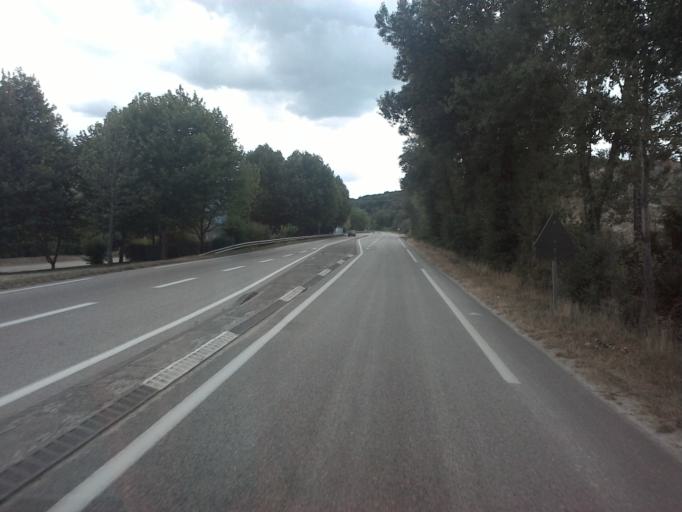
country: FR
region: Rhone-Alpes
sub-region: Departement de l'Ain
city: Sault-Brenaz
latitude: 45.8541
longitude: 5.4037
